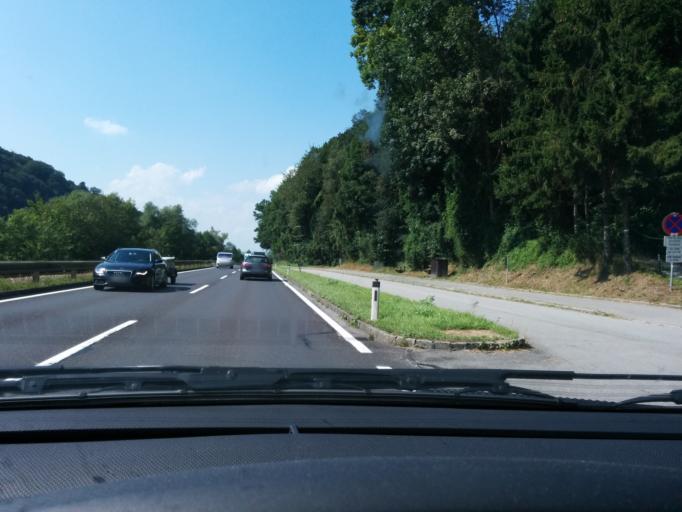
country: AT
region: Upper Austria
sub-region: Politischer Bezirk Urfahr-Umgebung
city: Ottensheim
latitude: 48.3148
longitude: 14.2146
